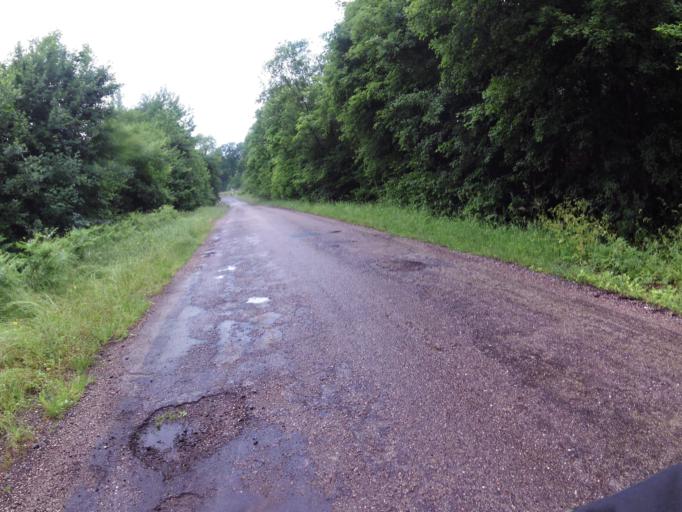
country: FR
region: Champagne-Ardenne
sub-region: Departement de la Marne
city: Sermaize-les-Bains
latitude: 48.7660
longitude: 4.9424
